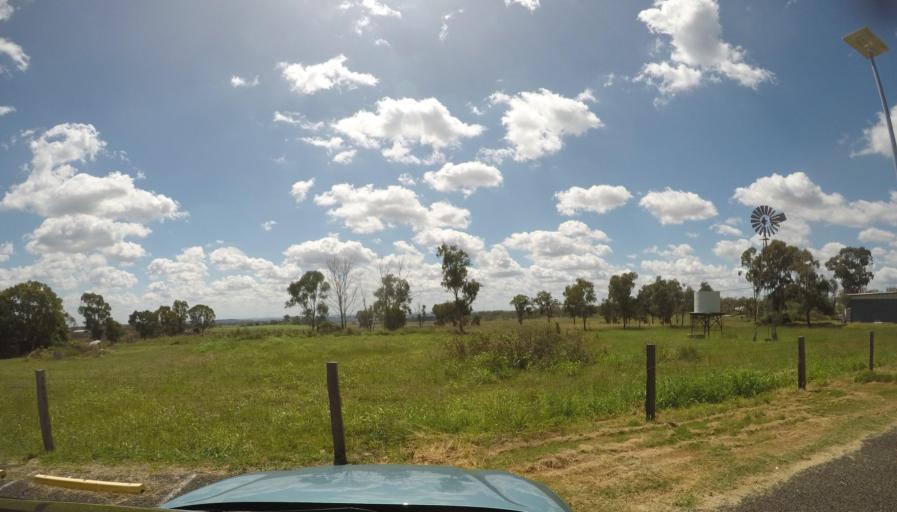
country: AU
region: Queensland
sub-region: Toowoomba
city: Oakey
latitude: -27.5561
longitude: 151.7190
